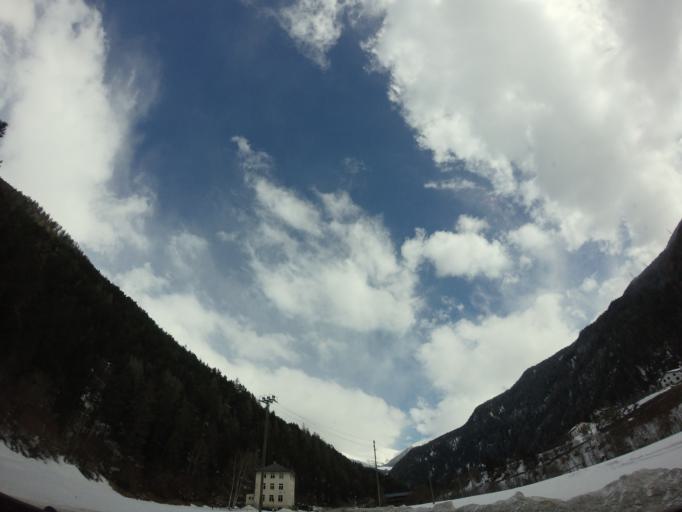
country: AT
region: Tyrol
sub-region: Politischer Bezirk Landeck
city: Nauders
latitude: 46.8682
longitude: 10.4419
